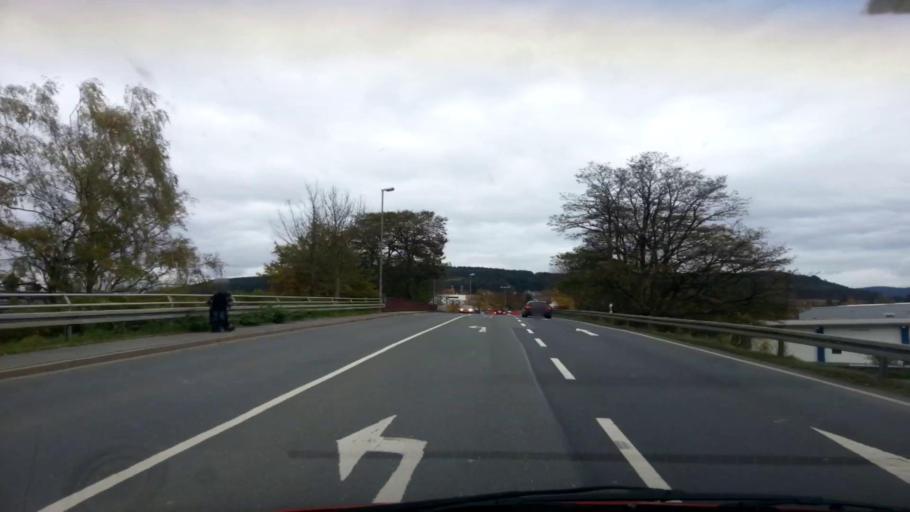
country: DE
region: Bavaria
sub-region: Upper Franconia
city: Kronach
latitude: 50.2334
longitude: 11.3279
